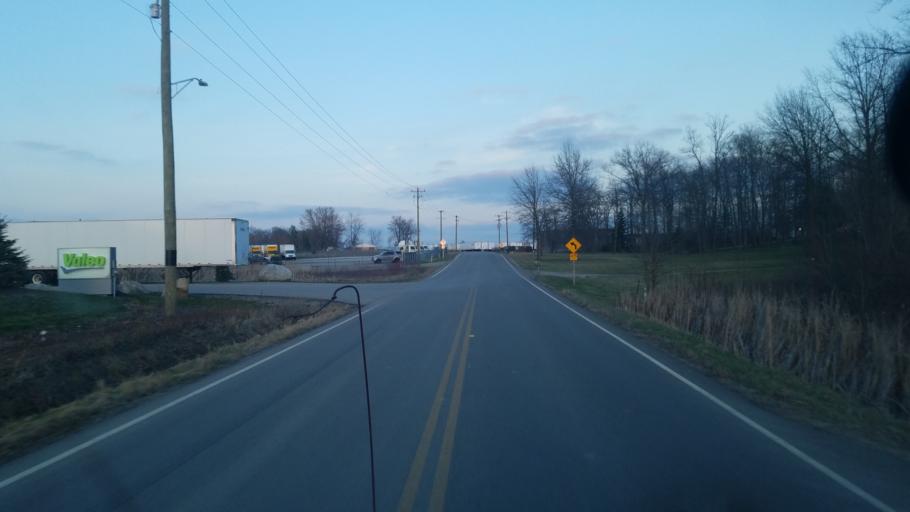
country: US
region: Ohio
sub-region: Champaign County
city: North Lewisburg
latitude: 40.2697
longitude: -83.5506
